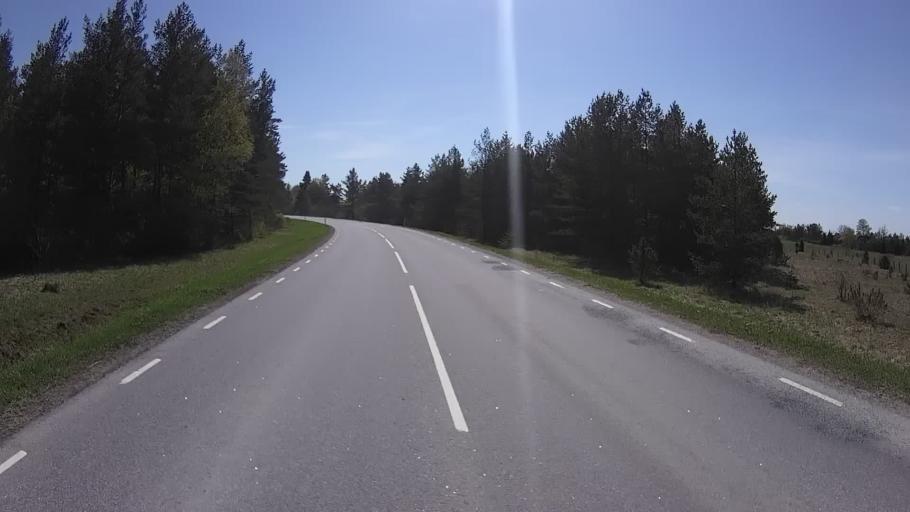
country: EE
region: Harju
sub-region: Keila linn
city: Keila
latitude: 59.3002
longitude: 24.3236
